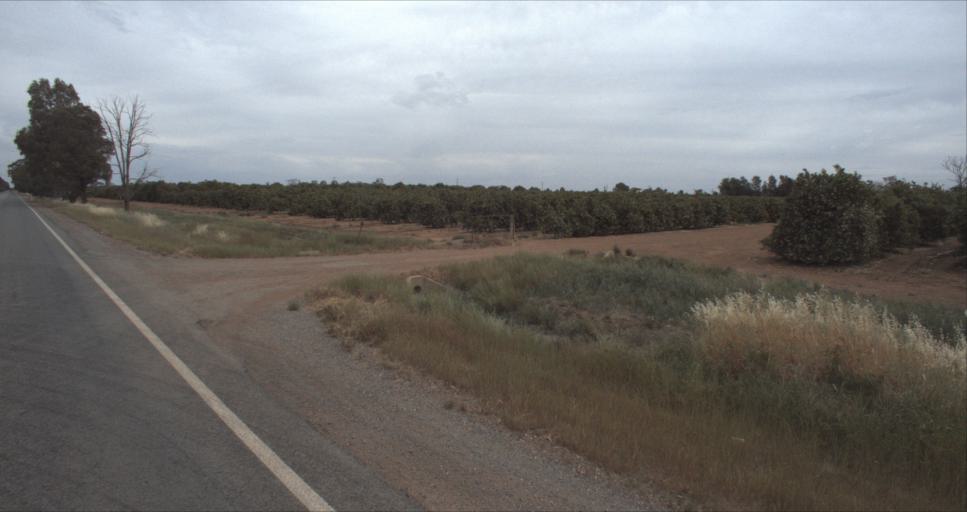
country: AU
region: New South Wales
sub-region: Leeton
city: Leeton
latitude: -34.5083
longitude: 146.4218
